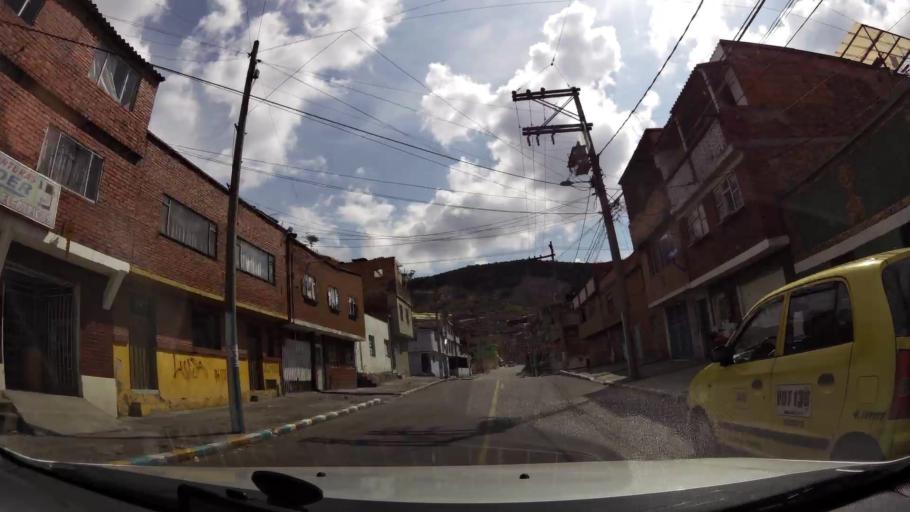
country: CO
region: Bogota D.C.
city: Bogota
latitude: 4.5641
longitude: -74.1007
